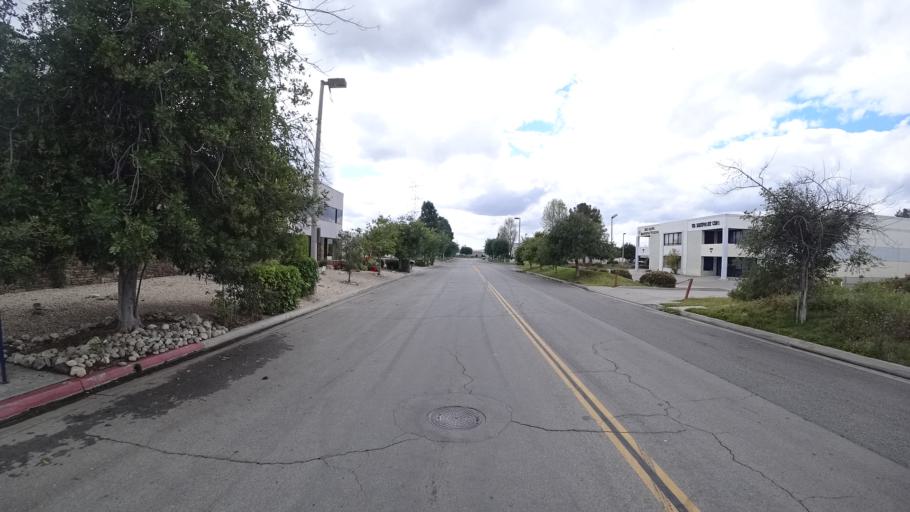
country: US
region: California
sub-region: Los Angeles County
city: Baldwin Park
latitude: 34.0974
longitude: -117.9825
